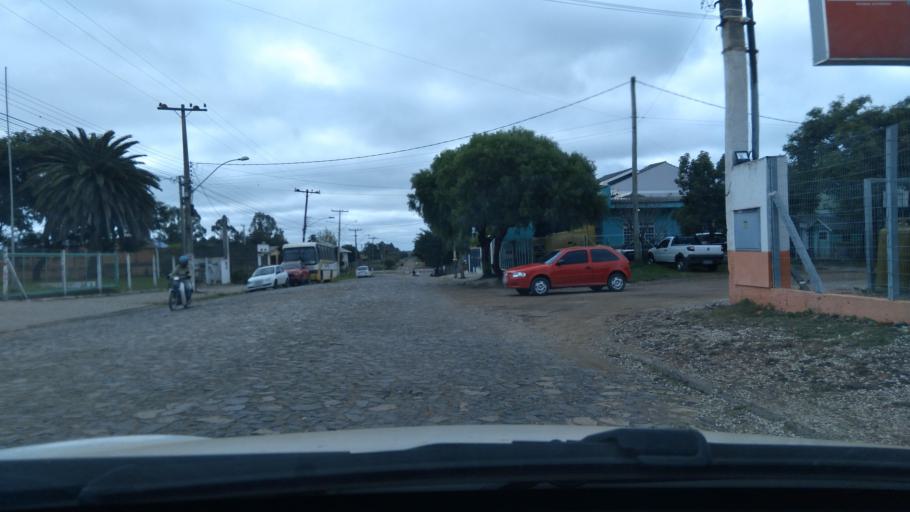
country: BR
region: Rio Grande do Sul
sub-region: Dom Pedrito
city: Dom Pedrito
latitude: -30.9651
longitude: -54.6724
